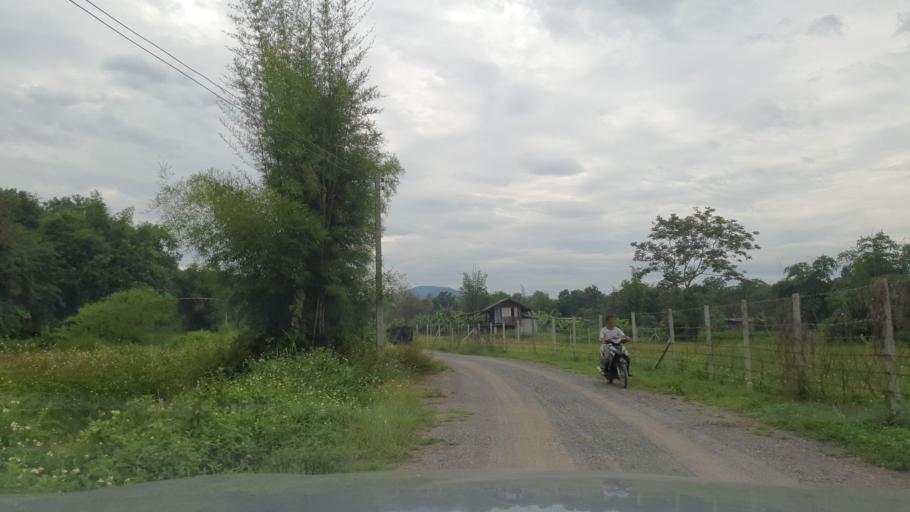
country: TH
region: Chiang Mai
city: San Sai
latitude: 18.9449
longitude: 98.9060
